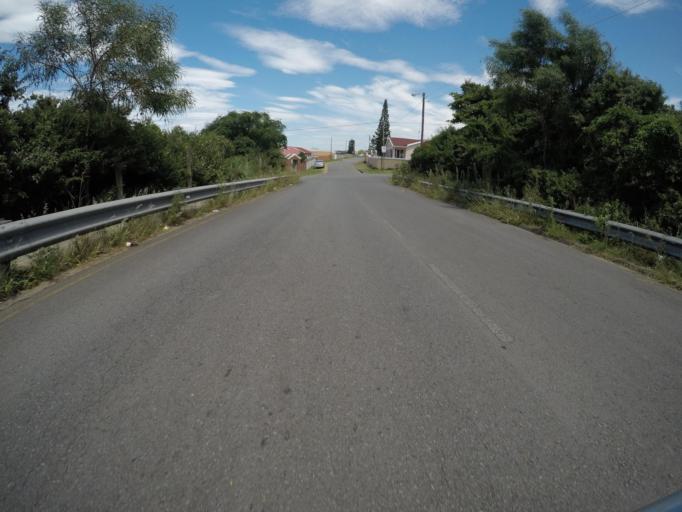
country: ZA
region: Eastern Cape
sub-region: Buffalo City Metropolitan Municipality
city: East London
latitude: -33.0408
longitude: 27.8670
